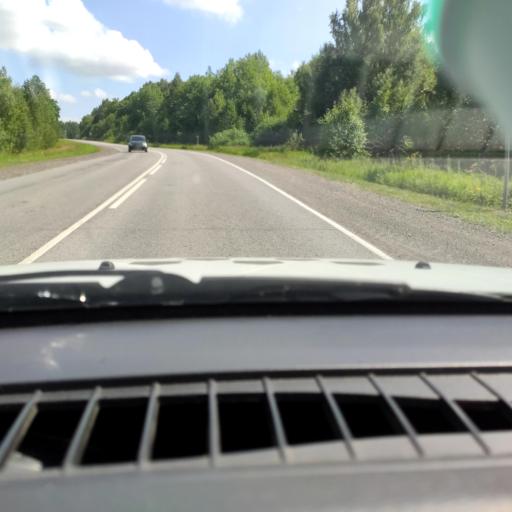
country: RU
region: Bashkortostan
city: Verkhniye Kigi
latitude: 55.3862
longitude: 58.6676
